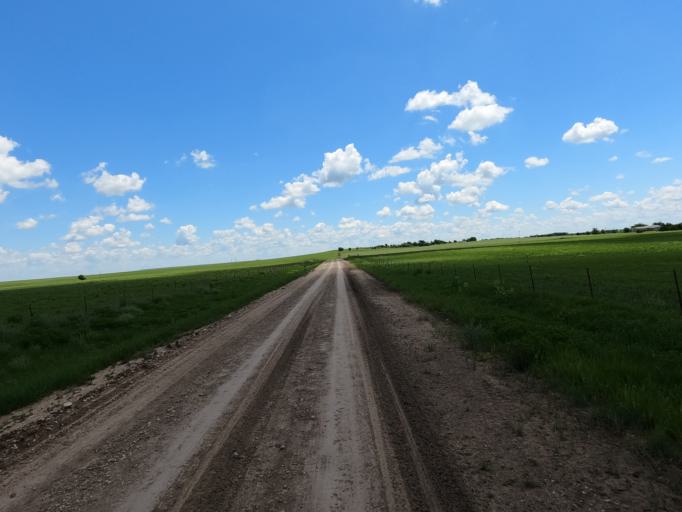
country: US
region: Kansas
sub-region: Marion County
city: Marion
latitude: 38.2309
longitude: -96.7899
